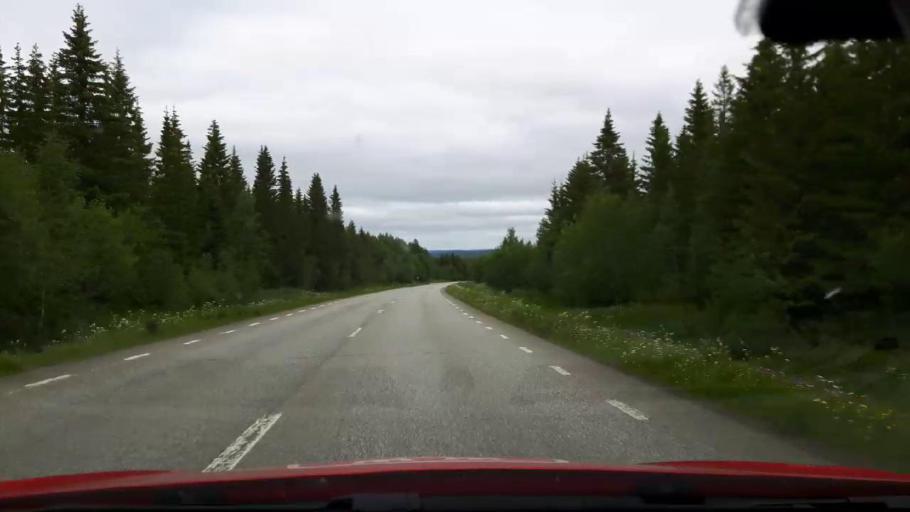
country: SE
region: Jaemtland
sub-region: Krokoms Kommun
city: Krokom
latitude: 63.5855
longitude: 14.6361
